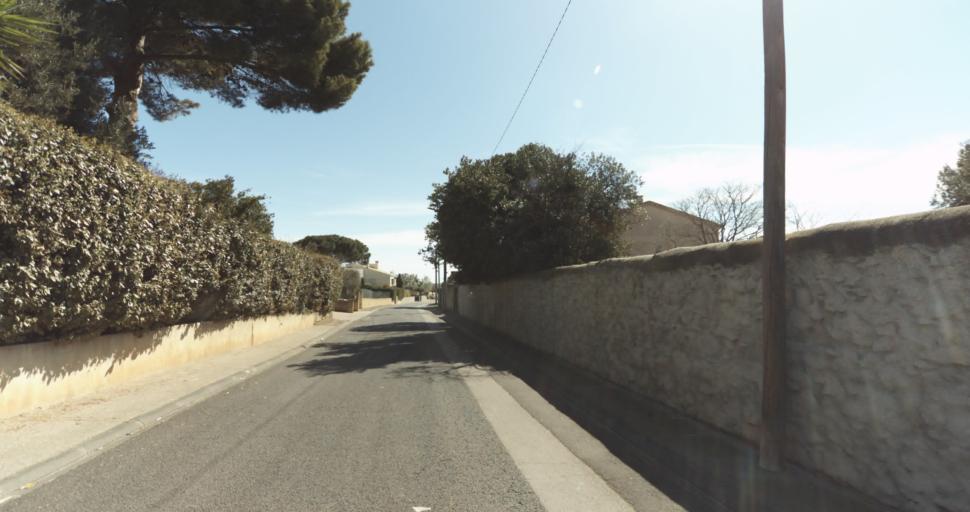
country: FR
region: Languedoc-Roussillon
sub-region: Departement de l'Herault
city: Marseillan
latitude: 43.3571
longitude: 3.5321
